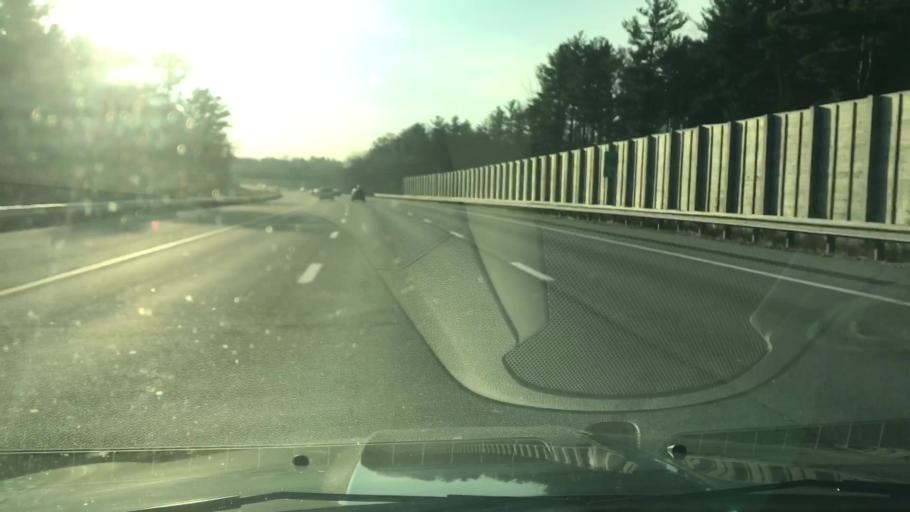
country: US
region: New Hampshire
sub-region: Rockingham County
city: Salem
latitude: 42.7642
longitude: -71.2373
